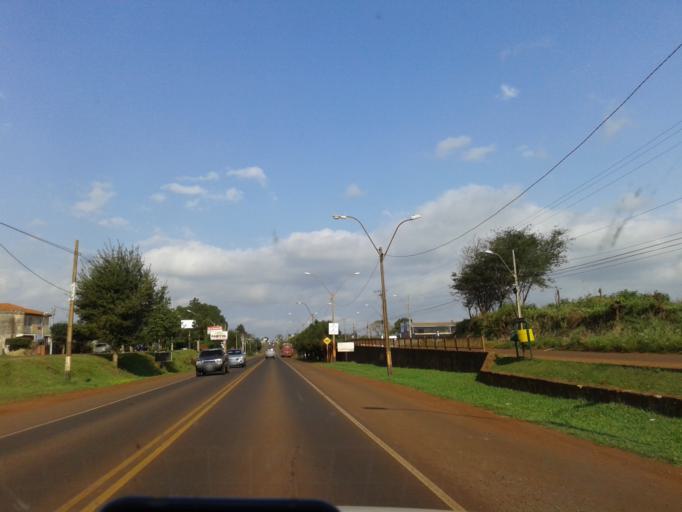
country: PY
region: Itapua
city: Arquitecto Tomas Romero Pereira
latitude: -26.5192
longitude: -55.2688
